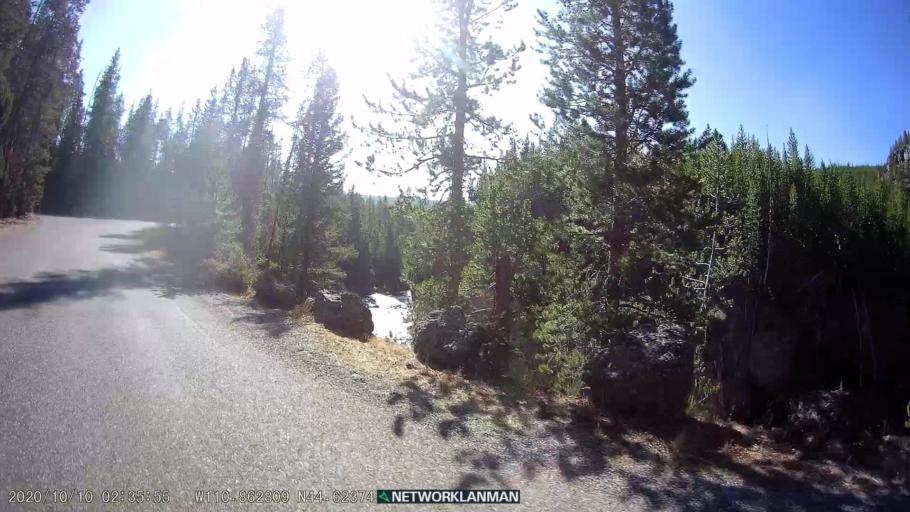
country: US
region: Montana
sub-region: Gallatin County
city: West Yellowstone
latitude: 44.6237
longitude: -110.8627
